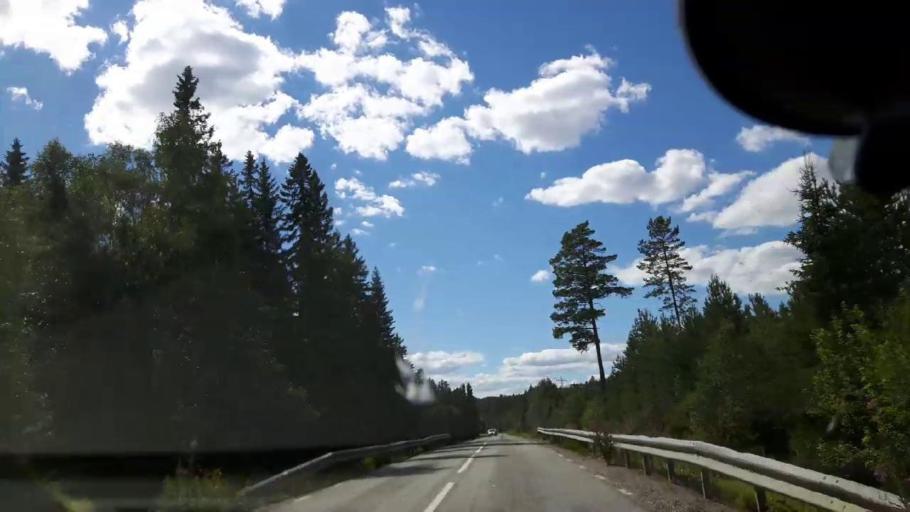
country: SE
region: Jaemtland
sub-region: Ragunda Kommun
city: Hammarstrand
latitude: 62.8568
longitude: 16.1997
